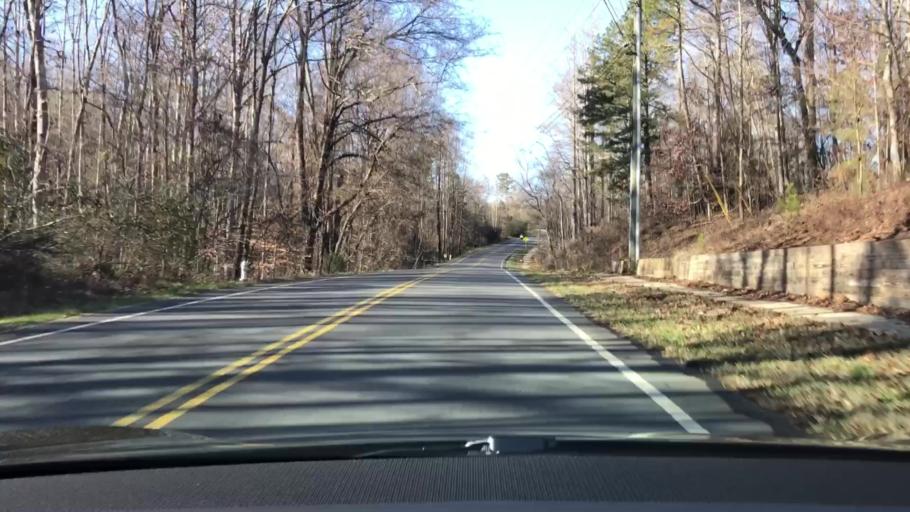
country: US
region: Georgia
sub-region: Barrow County
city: Auburn
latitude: 34.0662
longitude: -83.8533
